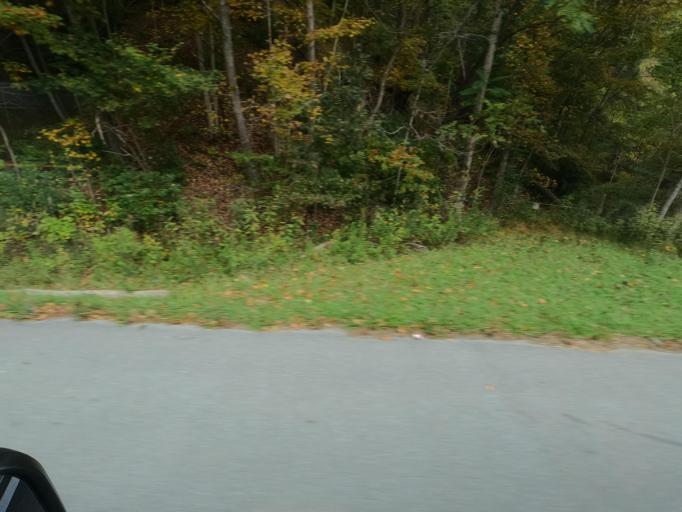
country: US
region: Tennessee
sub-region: Carter County
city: Elizabethton
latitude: 36.2451
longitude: -82.1927
